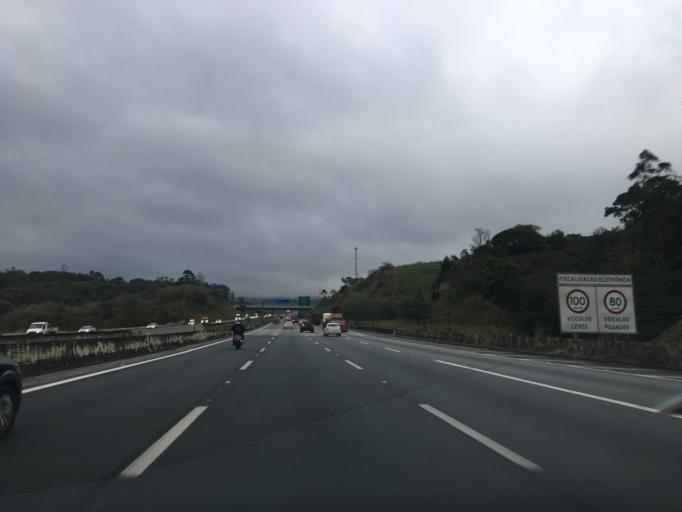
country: BR
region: Sao Paulo
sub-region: Caieiras
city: Caieiras
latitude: -23.4360
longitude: -46.7640
